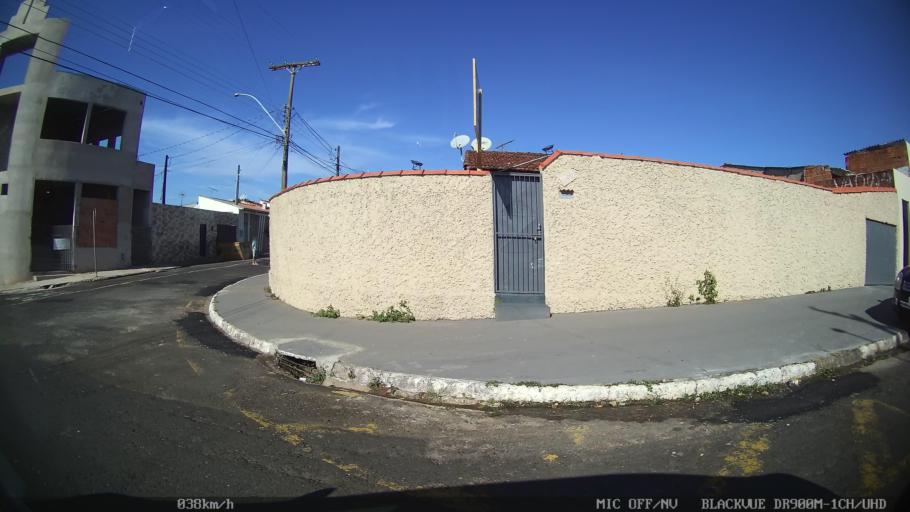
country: BR
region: Sao Paulo
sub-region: Franca
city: Franca
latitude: -20.4981
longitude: -47.4118
